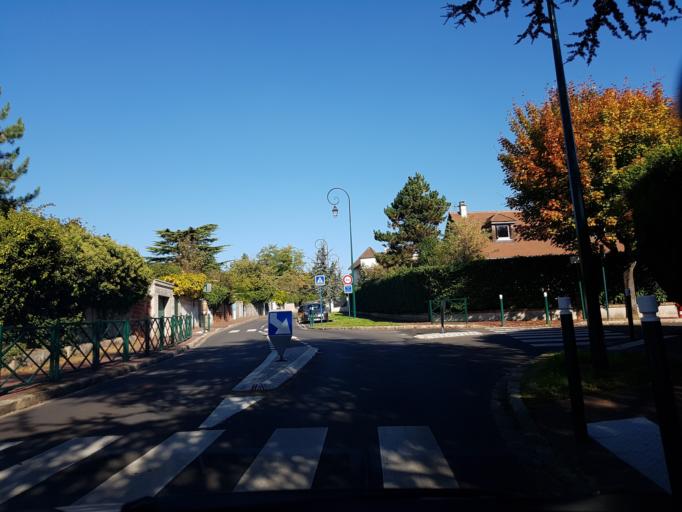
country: FR
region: Ile-de-France
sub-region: Departement du Val-de-Marne
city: Boissy-Saint-Leger
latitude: 48.7655
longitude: 2.5143
